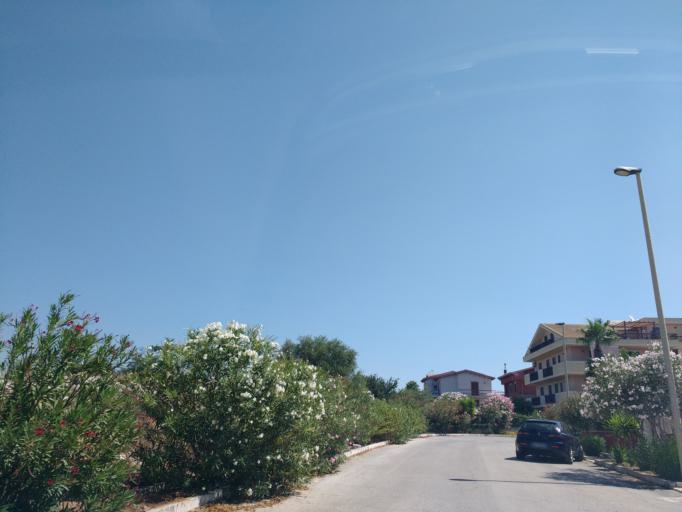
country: IT
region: Sicily
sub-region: Ragusa
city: Pozzallo
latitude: 36.7348
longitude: 14.8518
